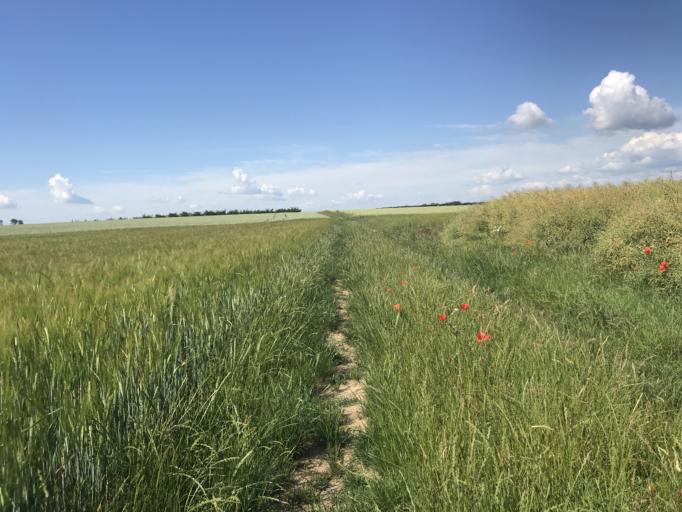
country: DE
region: Rheinland-Pfalz
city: Essenheim
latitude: 49.9413
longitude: 8.1293
